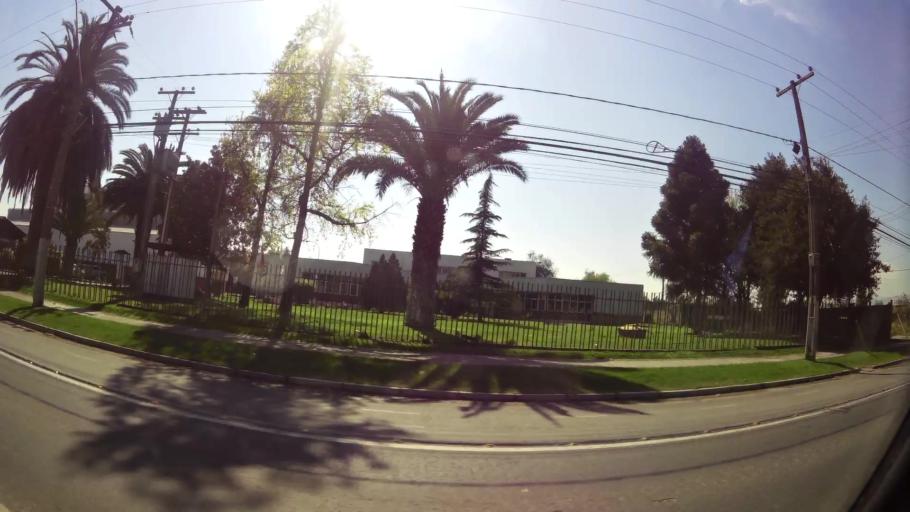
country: CL
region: Santiago Metropolitan
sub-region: Provincia de Talagante
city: Penaflor
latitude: -33.5614
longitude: -70.8221
